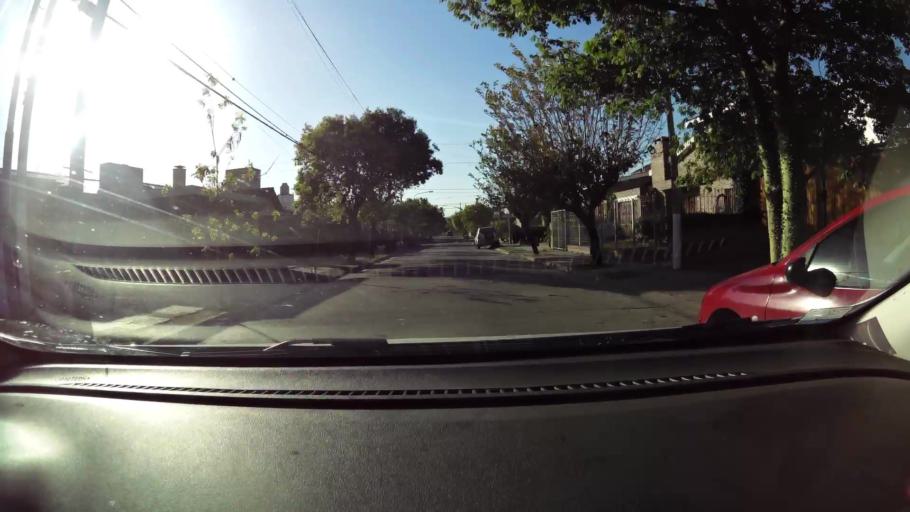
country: AR
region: Cordoba
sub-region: Departamento de Capital
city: Cordoba
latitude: -31.3804
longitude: -64.2357
